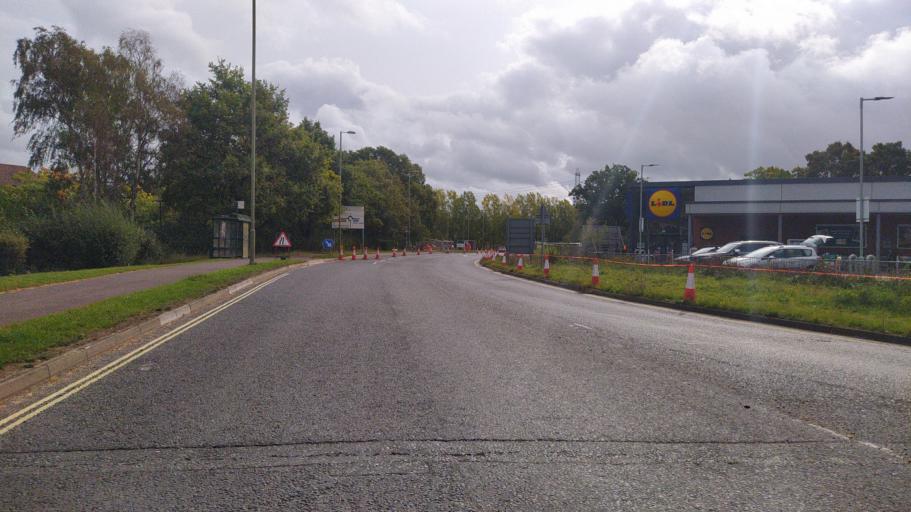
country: GB
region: England
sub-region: Hampshire
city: Botley
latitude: 50.8793
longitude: -1.2506
